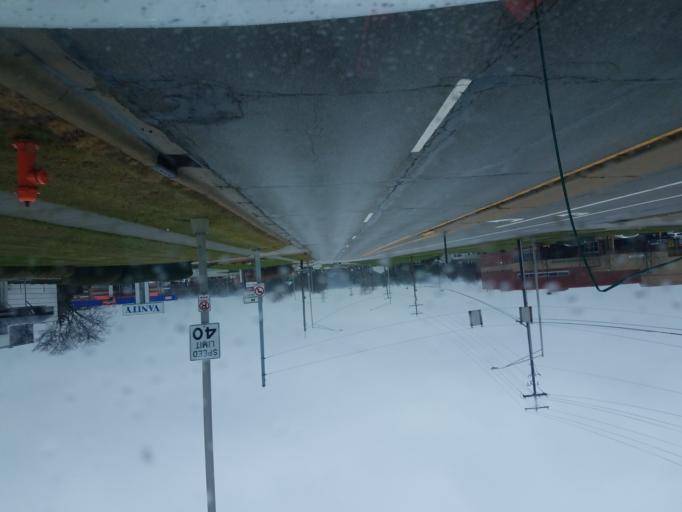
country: US
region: Ohio
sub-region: Franklin County
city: Dublin
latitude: 40.0651
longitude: -83.0942
